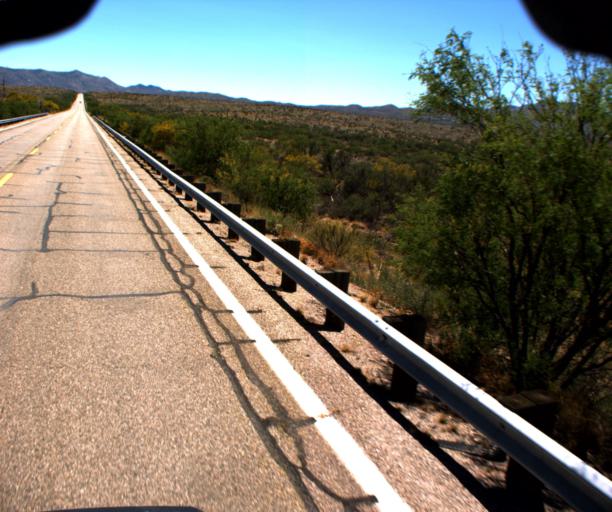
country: US
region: Arizona
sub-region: Pima County
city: Vail
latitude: 31.9866
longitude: -110.6816
